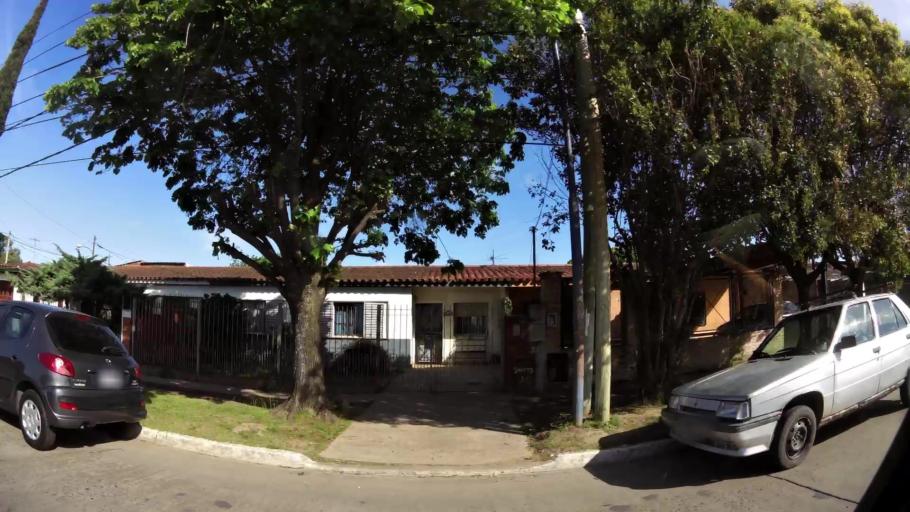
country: AR
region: Buenos Aires
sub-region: Partido de Quilmes
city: Quilmes
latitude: -34.7908
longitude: -58.2285
